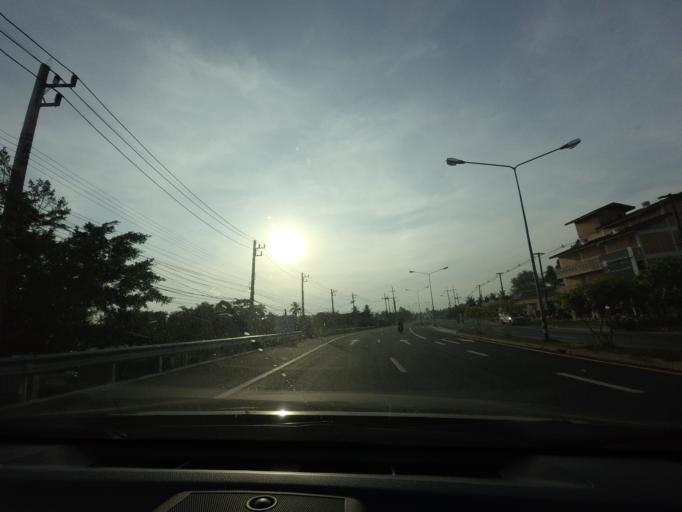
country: TH
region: Narathiwat
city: Narathiwat
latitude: 6.4169
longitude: 101.8438
